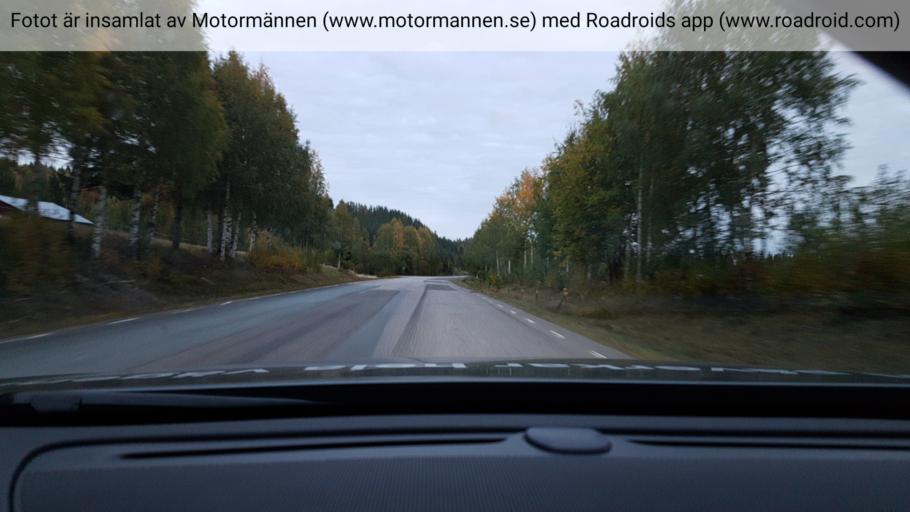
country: SE
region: Norrbotten
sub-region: Alvsbyns Kommun
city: AElvsbyn
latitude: 65.8531
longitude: 20.4412
